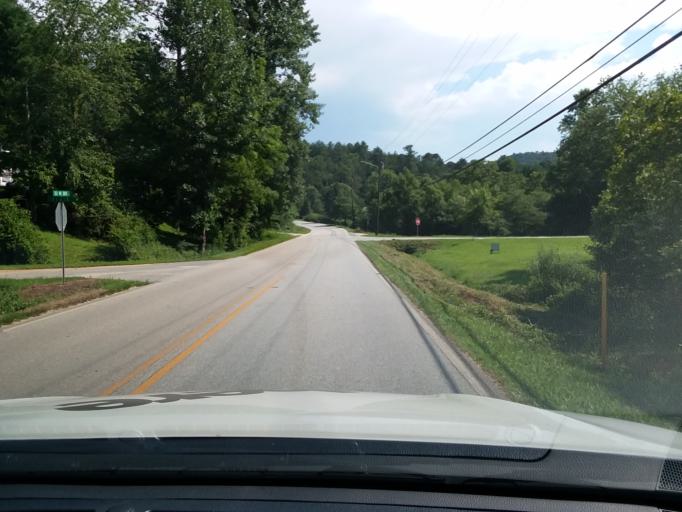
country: US
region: Georgia
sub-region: Rabun County
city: Clayton
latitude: 34.8425
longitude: -83.4361
